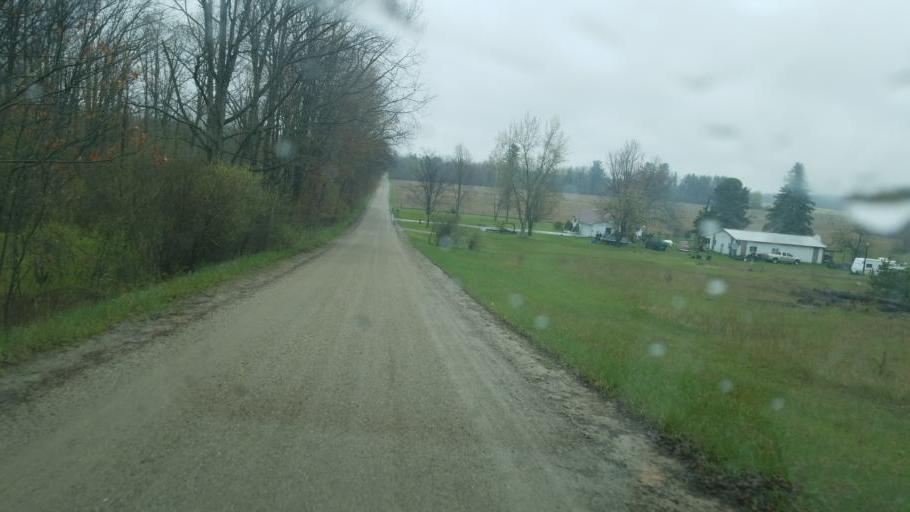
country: US
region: Michigan
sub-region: Montcalm County
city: Lakeview
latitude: 43.4552
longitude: -85.3132
